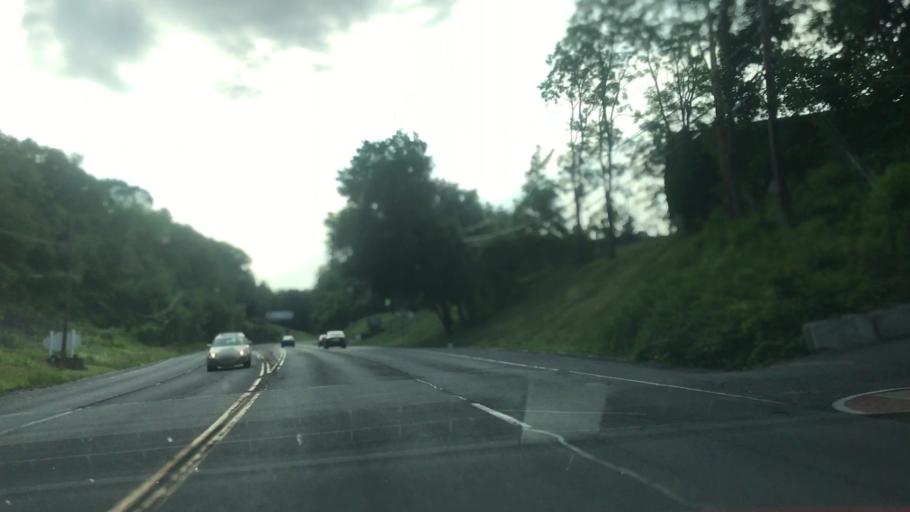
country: US
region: New York
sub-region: Albany County
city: Watervliet
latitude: 42.7340
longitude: -73.7154
